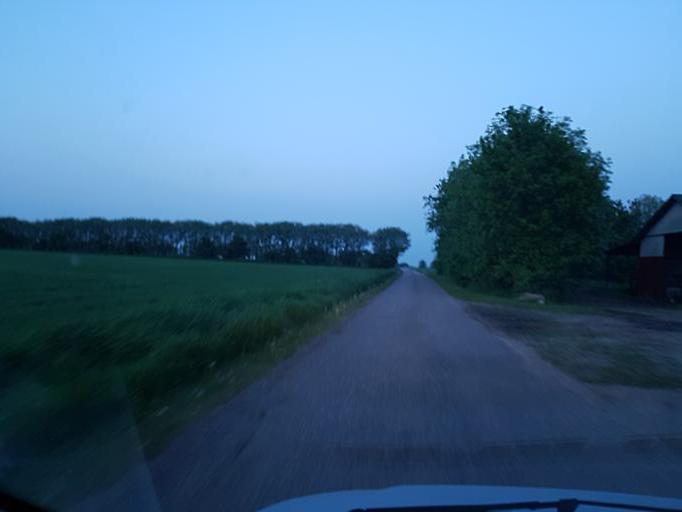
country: DK
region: South Denmark
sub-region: Esbjerg Kommune
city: Tjaereborg
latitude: 55.5103
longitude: 8.5659
